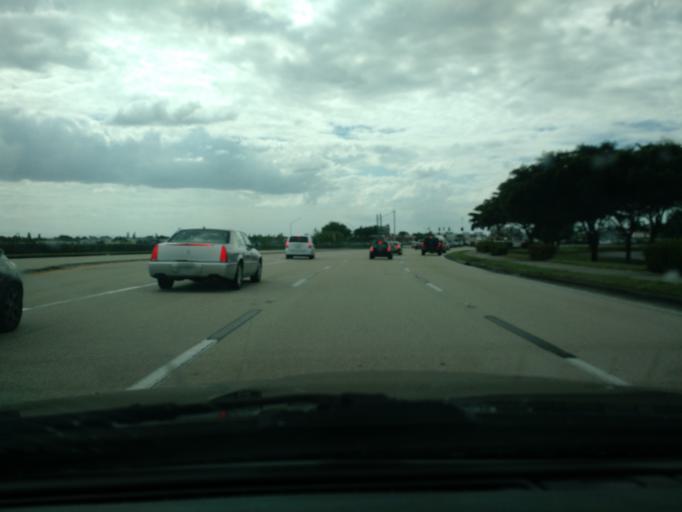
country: US
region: Florida
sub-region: Lee County
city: Pine Manor
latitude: 26.5836
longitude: -81.8698
